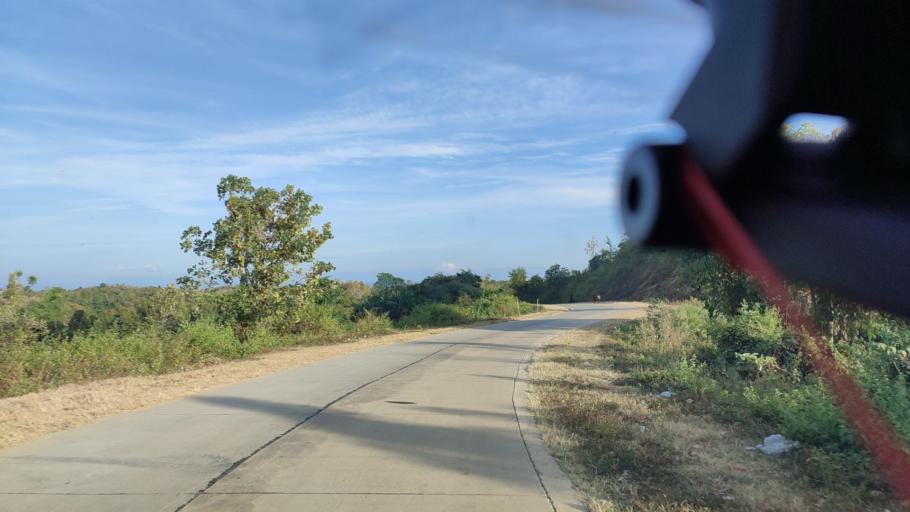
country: MM
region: Magway
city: Taungdwingyi
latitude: 20.0183
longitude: 95.8033
